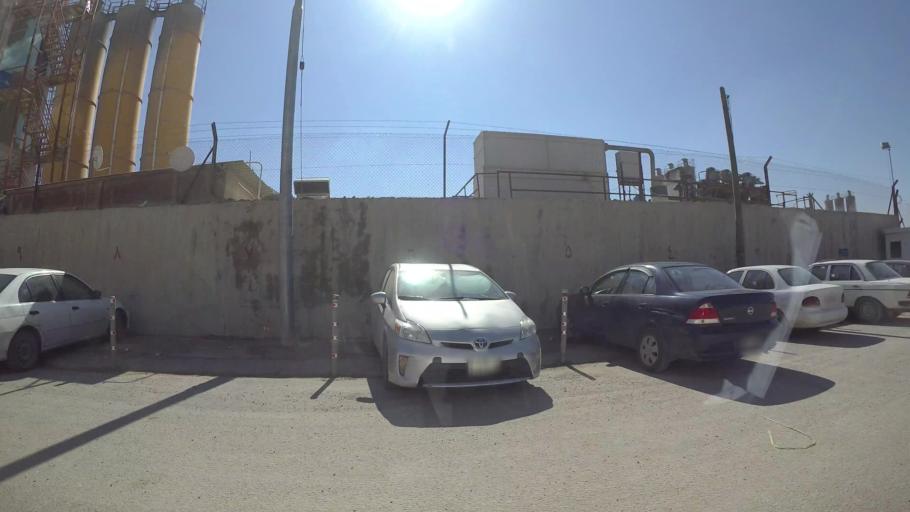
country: JO
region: Amman
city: Al Bunayyat ash Shamaliyah
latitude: 31.9130
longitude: 35.9131
